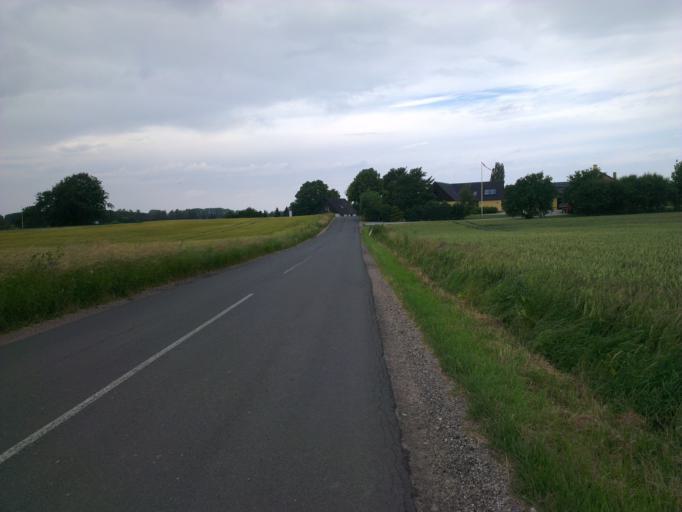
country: DK
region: Capital Region
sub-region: Frederikssund Kommune
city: Skibby
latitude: 55.7674
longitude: 11.9479
